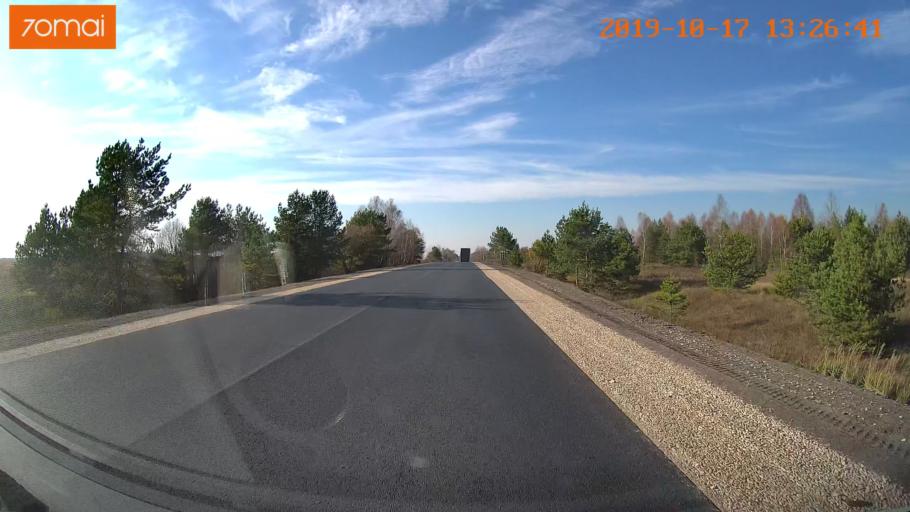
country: RU
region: Rjazan
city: Gus'-Zheleznyy
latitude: 55.1111
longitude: 40.9145
